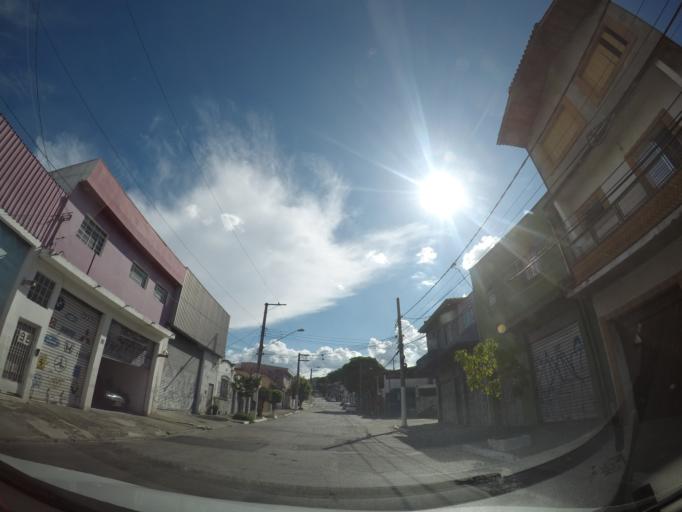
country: BR
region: Sao Paulo
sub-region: Sao Paulo
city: Sao Paulo
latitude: -23.5529
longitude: -46.5777
